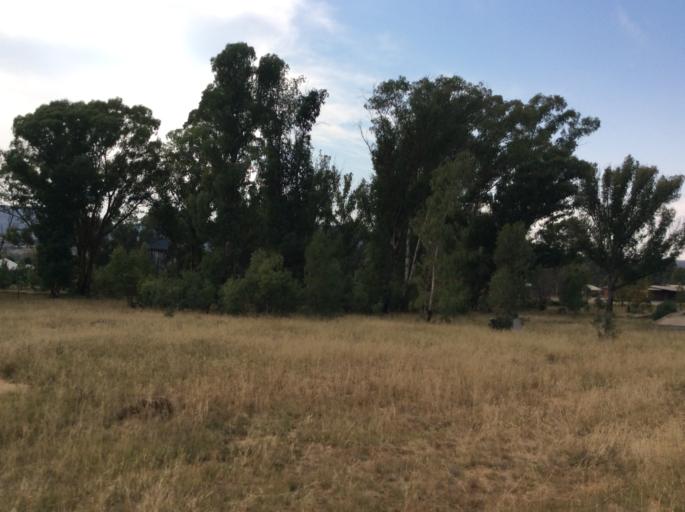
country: LS
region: Mafeteng
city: Mafeteng
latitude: -29.7323
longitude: 27.0246
